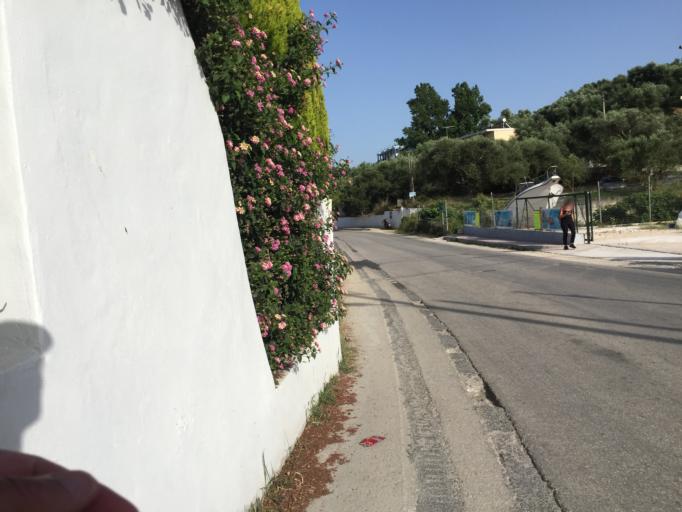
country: GR
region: Ionian Islands
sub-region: Nomos Zakynthou
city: Vanaton
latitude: 37.8201
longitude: 20.8570
